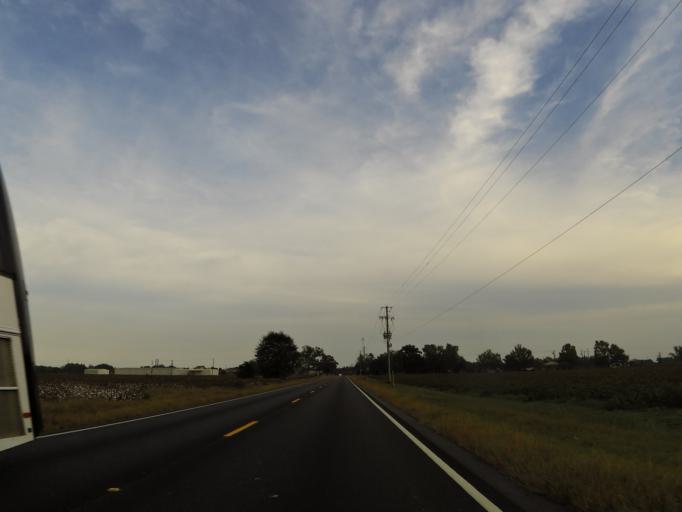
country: US
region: Alabama
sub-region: Escambia County
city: Atmore
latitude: 31.2234
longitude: -87.4746
